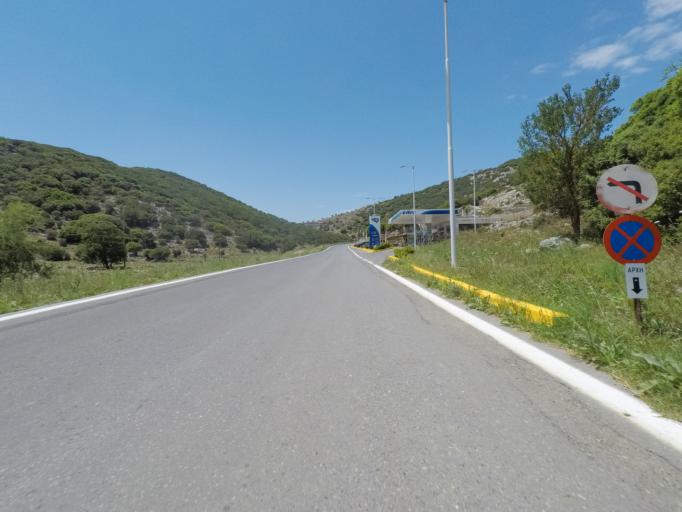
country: GR
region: Crete
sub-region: Nomos Irakleiou
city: Mokhos
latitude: 35.1990
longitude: 25.4612
